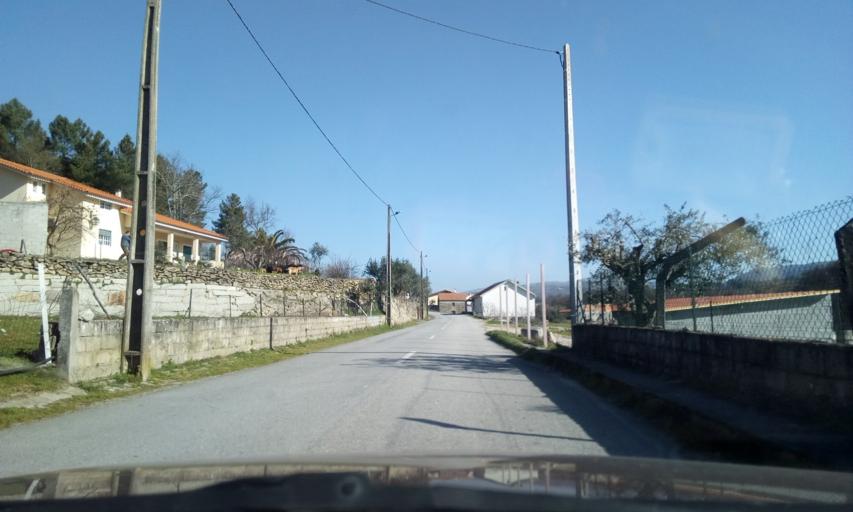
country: PT
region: Guarda
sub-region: Celorico da Beira
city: Celorico da Beira
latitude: 40.6510
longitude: -7.4658
